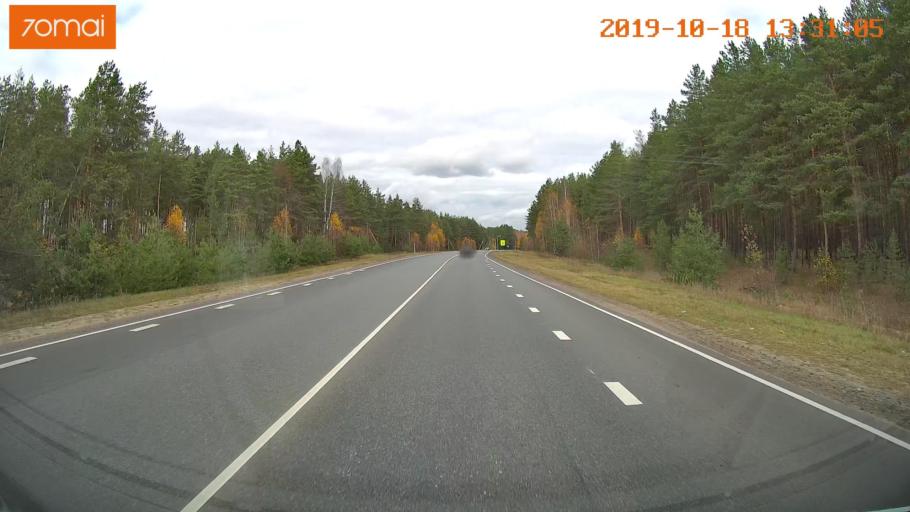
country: RU
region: Rjazan
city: Solotcha
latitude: 54.8179
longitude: 39.8949
